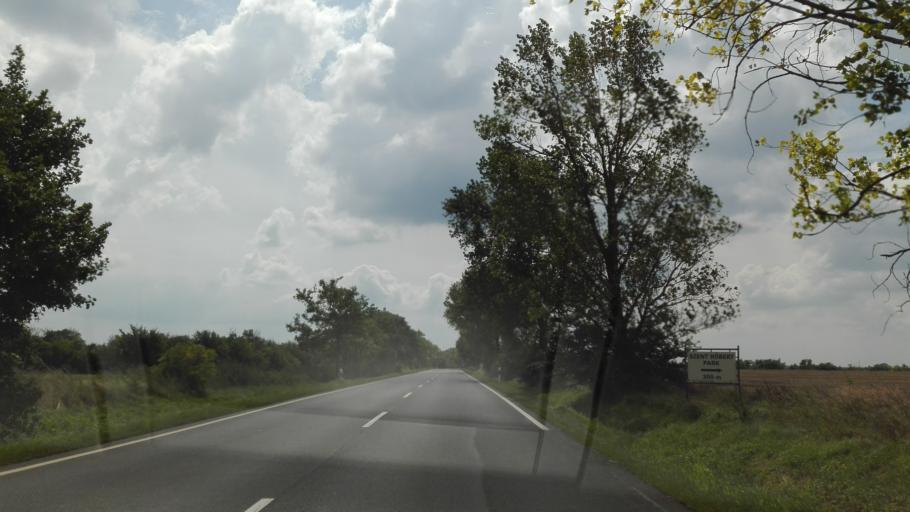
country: HU
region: Fejer
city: Eloszallas
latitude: 46.8194
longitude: 18.7930
